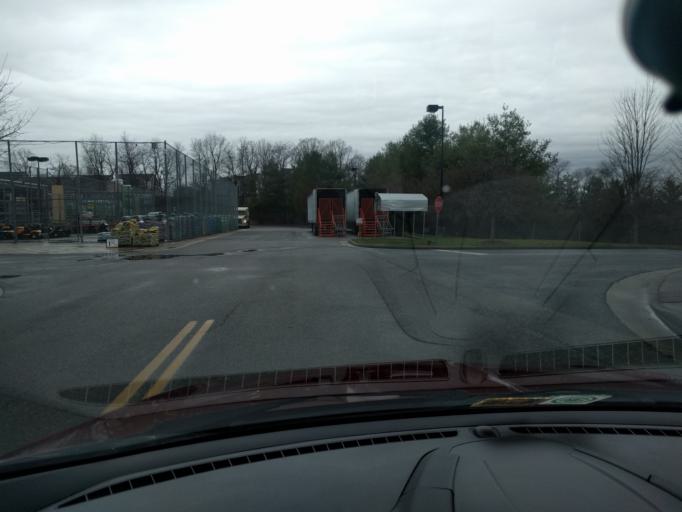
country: US
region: Virginia
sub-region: Montgomery County
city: Merrimac
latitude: 37.1578
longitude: -80.4247
